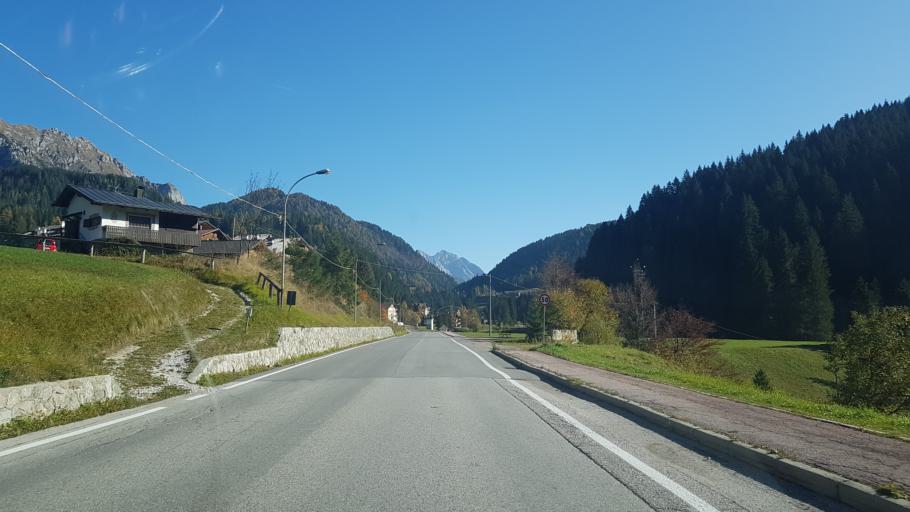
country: IT
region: Veneto
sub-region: Provincia di Belluno
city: Granvilla
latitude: 46.5688
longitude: 12.7050
